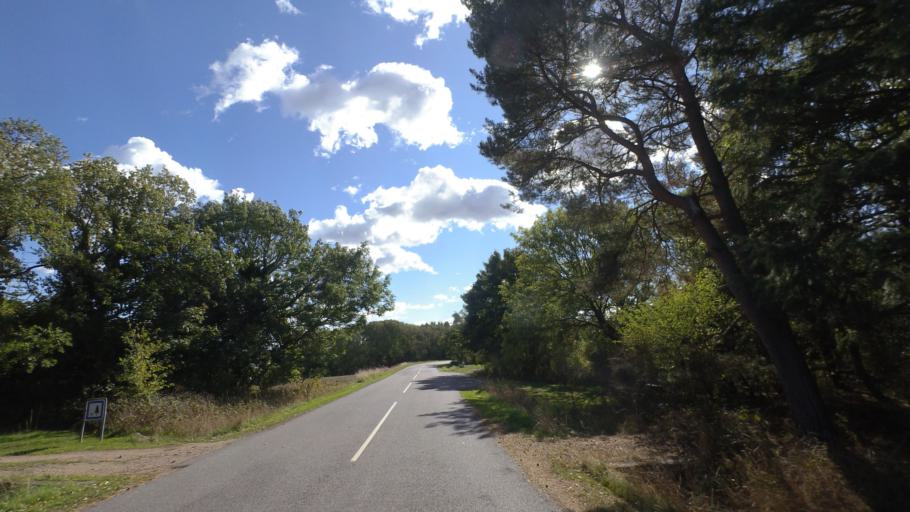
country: DK
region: Capital Region
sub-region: Bornholm Kommune
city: Nexo
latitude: 55.0682
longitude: 15.0830
